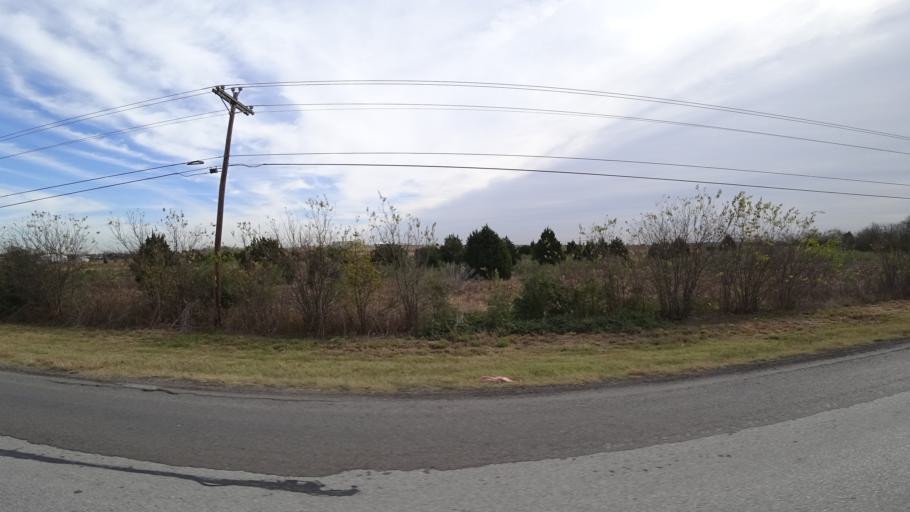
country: US
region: Texas
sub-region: Travis County
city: Onion Creek
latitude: 30.1393
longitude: -97.6964
